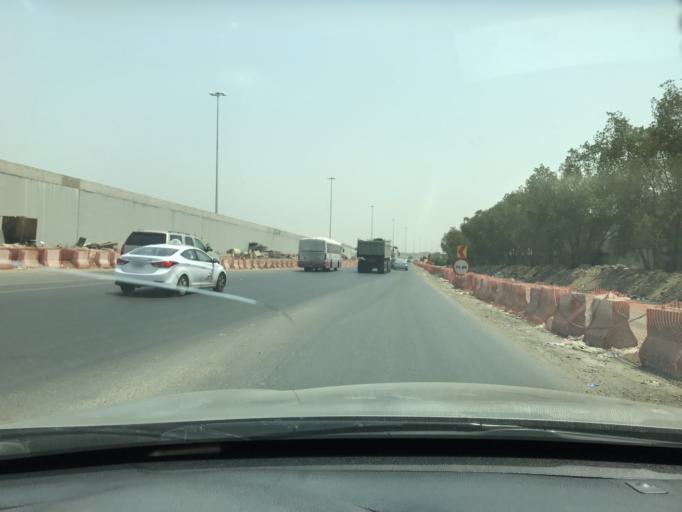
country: SA
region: Makkah
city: Jeddah
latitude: 21.6135
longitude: 39.2414
